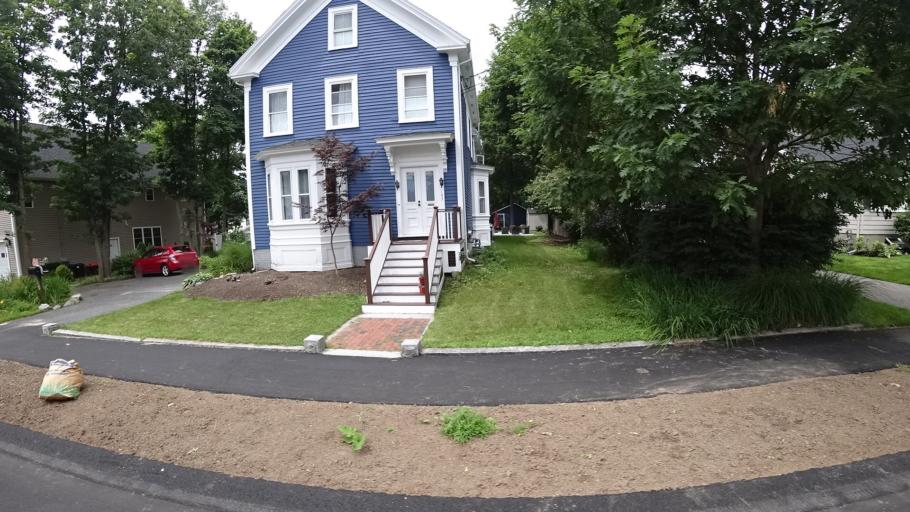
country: US
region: Massachusetts
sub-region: Norfolk County
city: Dedham
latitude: 42.2370
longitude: -71.1490
